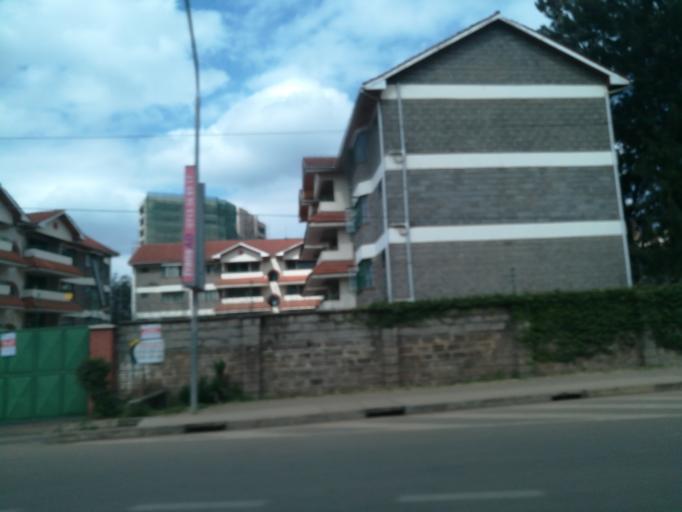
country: KE
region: Nairobi Area
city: Nairobi
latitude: -1.2861
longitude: 36.7878
